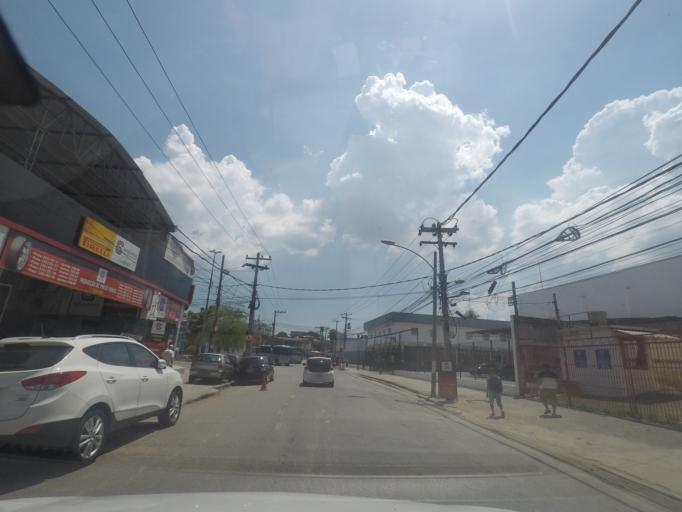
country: BR
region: Rio de Janeiro
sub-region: Rio De Janeiro
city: Rio de Janeiro
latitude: -22.8672
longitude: -43.2571
